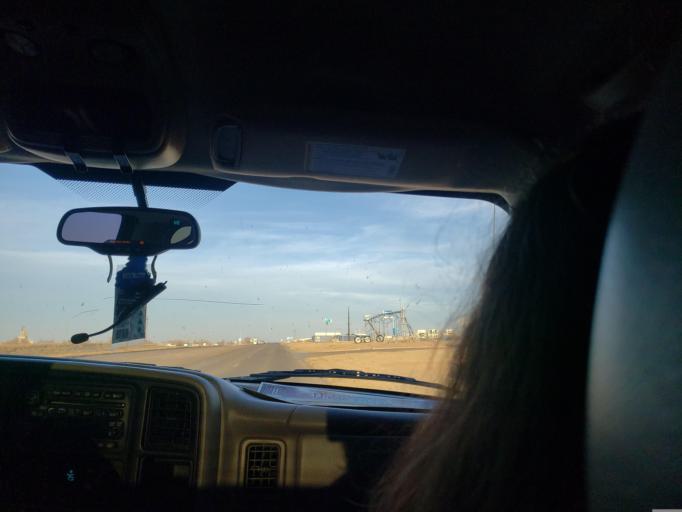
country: US
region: Oklahoma
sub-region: Texas County
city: Guymon
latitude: 36.6948
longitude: -101.4604
